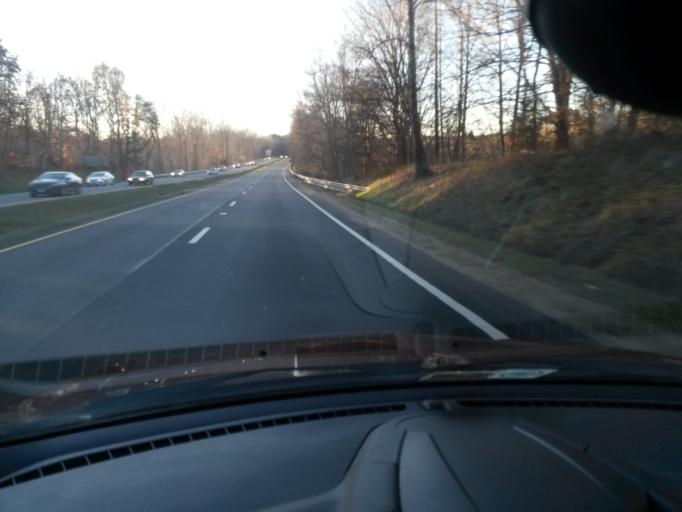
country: US
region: Virginia
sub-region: Franklin County
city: Rocky Mount
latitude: 37.0025
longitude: -79.8703
